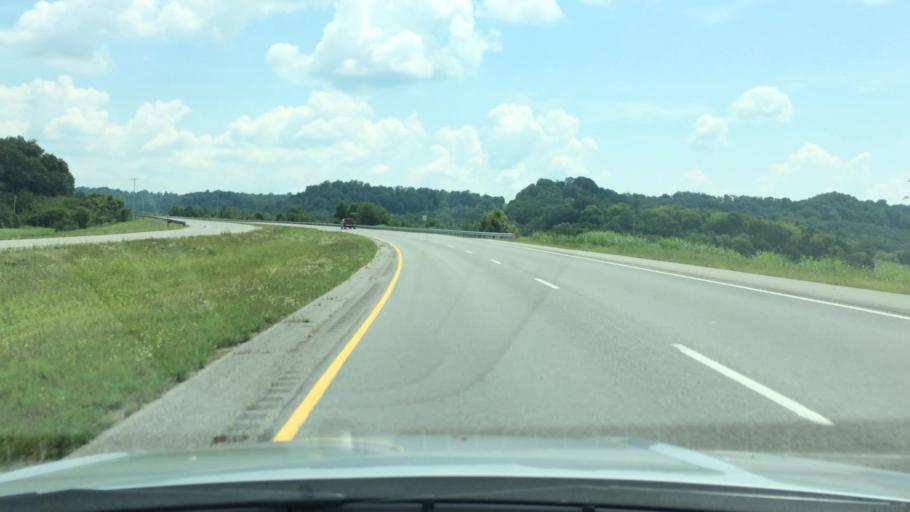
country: US
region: Tennessee
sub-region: Giles County
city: Pulaski
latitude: 35.1810
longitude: -86.9291
